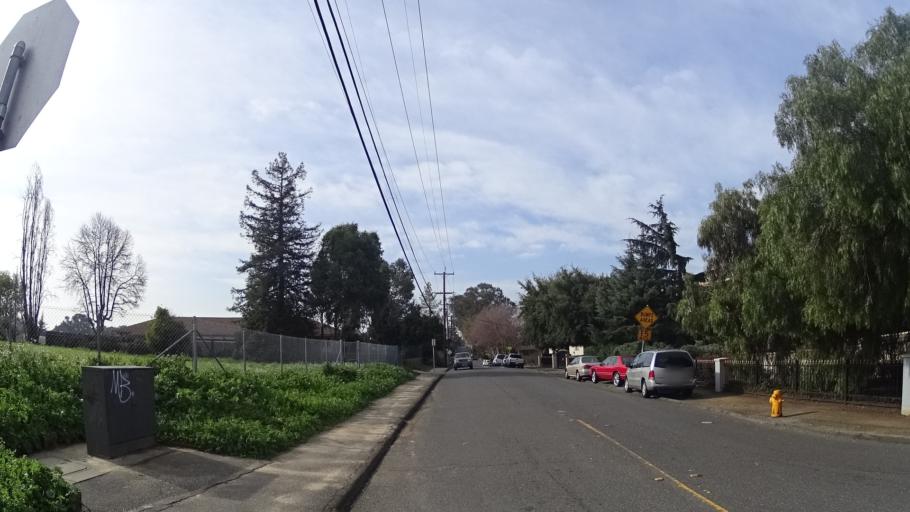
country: US
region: California
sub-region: Alameda County
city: Hayward
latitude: 37.6701
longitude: -122.0725
